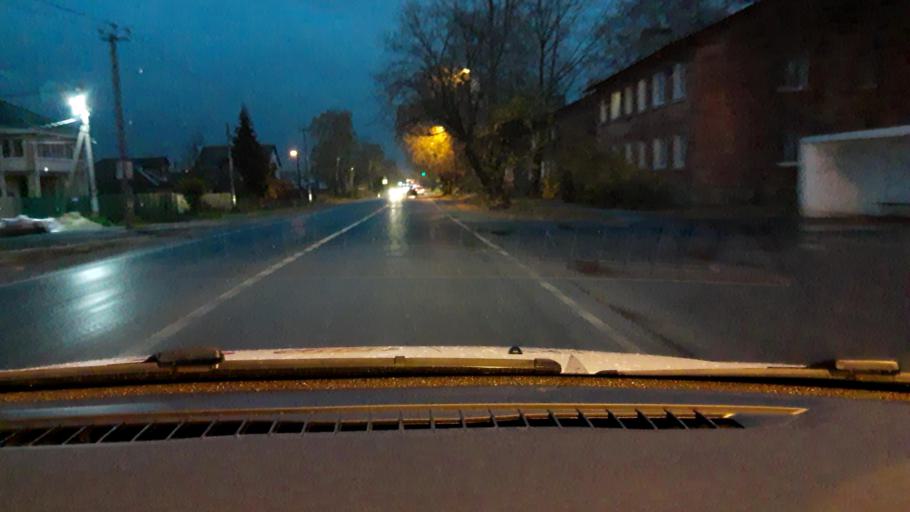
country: RU
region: Nizjnij Novgorod
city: Bor
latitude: 56.3635
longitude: 44.0677
